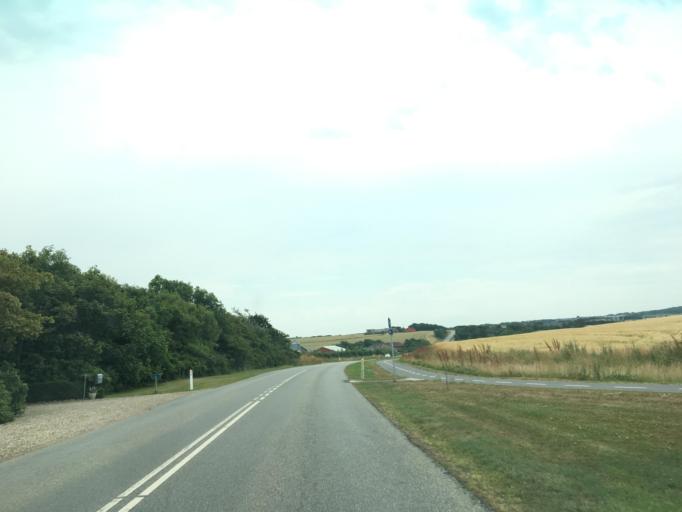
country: DK
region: North Denmark
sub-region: Thisted Kommune
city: Hurup
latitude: 56.7752
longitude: 8.4234
